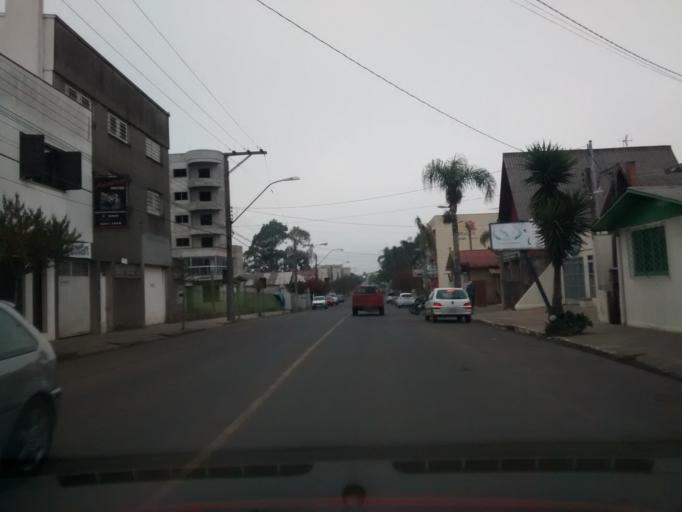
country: BR
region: Rio Grande do Sul
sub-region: Vacaria
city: Vacaria
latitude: -28.5048
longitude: -50.9340
